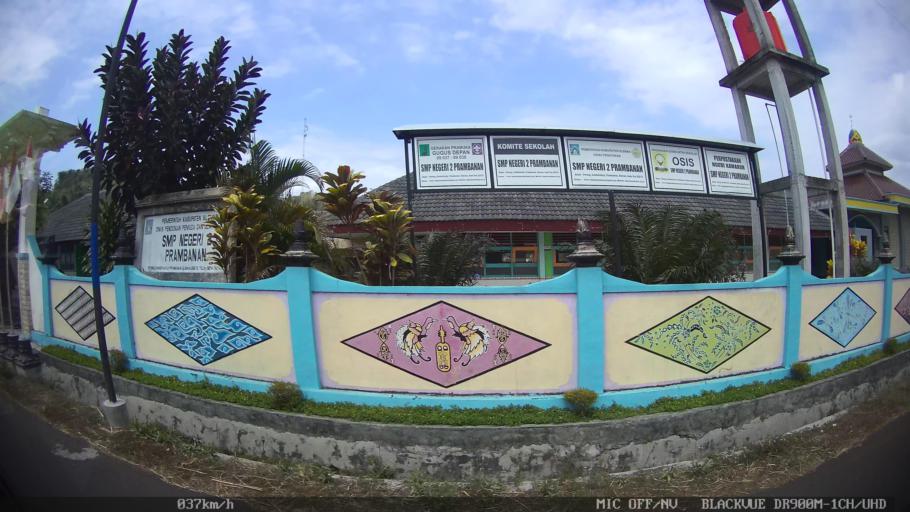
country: ID
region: Central Java
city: Candi Prambanan
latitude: -7.8112
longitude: 110.5055
